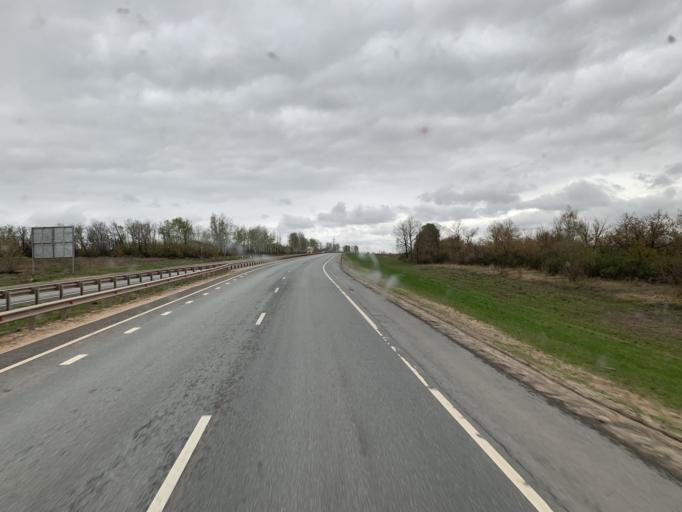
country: RU
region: Ulyanovsk
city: Kanadey
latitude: 53.1441
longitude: 47.5339
